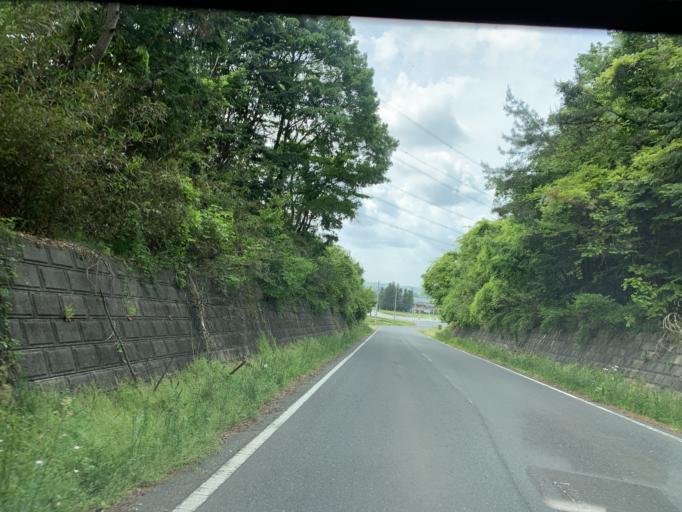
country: JP
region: Iwate
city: Ichinoseki
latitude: 38.8048
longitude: 141.0105
